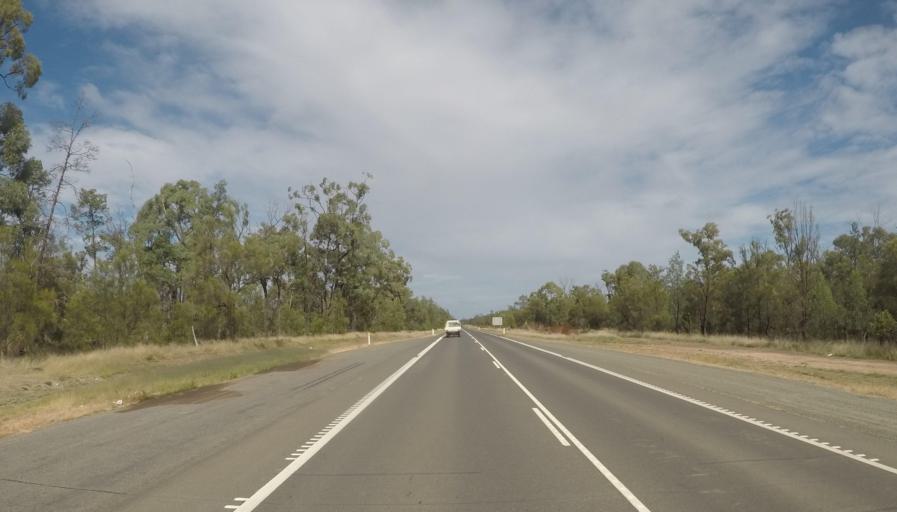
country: AU
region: Queensland
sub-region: Western Downs
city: Westcourt
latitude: -26.6220
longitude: 149.5072
